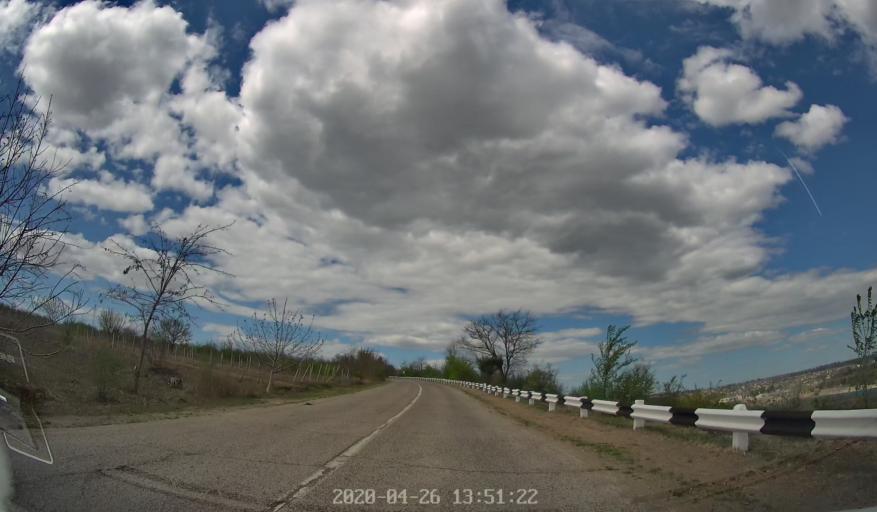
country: MD
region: Telenesti
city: Dubasari
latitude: 47.2667
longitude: 29.1243
